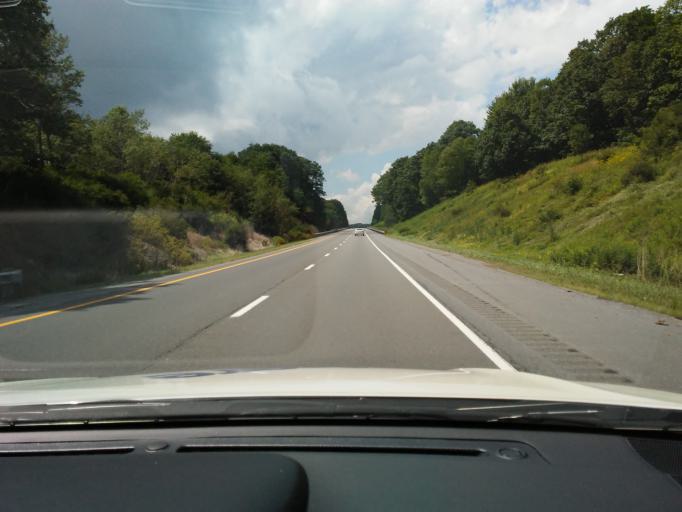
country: US
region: Pennsylvania
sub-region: Clearfield County
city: DuBois
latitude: 41.1374
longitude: -78.7321
